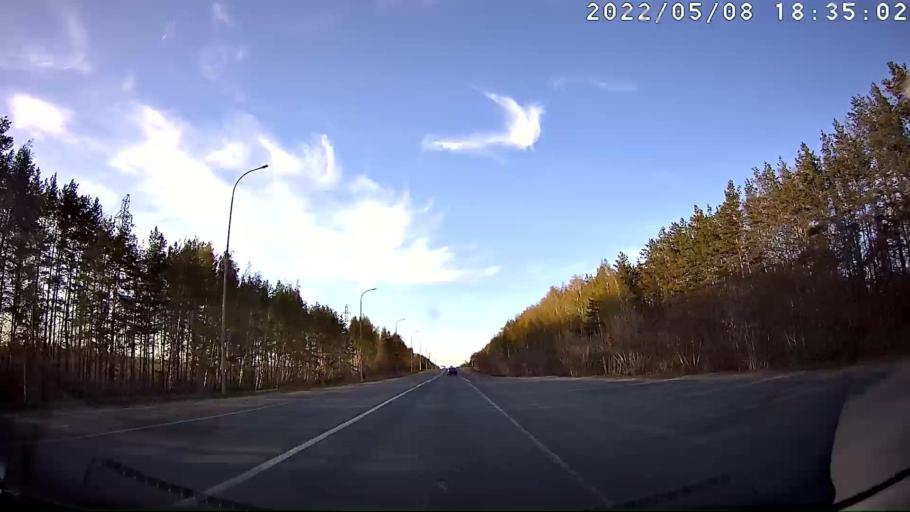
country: RU
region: Mariy-El
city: Volzhsk
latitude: 55.9047
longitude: 48.3585
